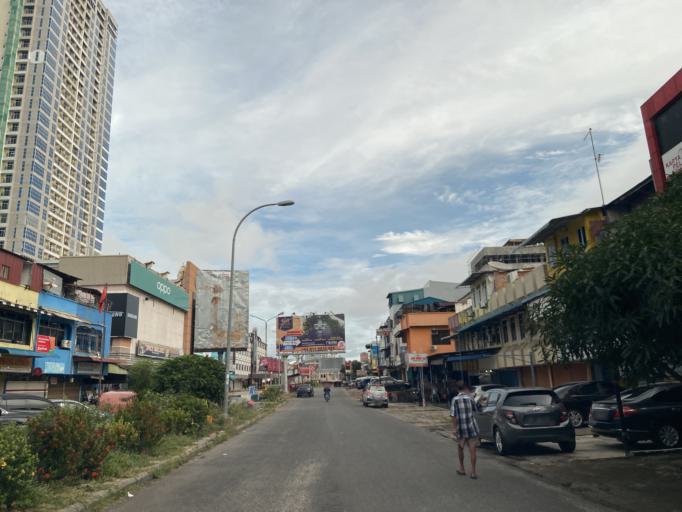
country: SG
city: Singapore
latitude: 1.1437
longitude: 104.0113
